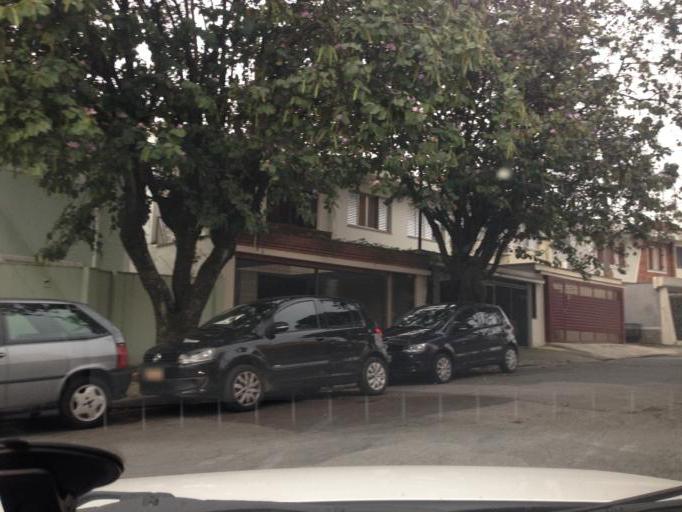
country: BR
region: Sao Paulo
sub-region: Osasco
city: Osasco
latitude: -23.5298
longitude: -46.7197
